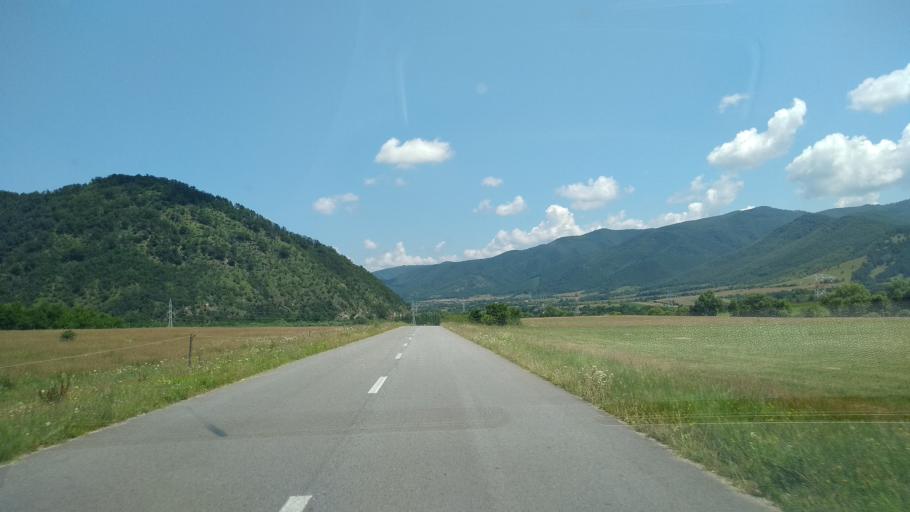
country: RO
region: Hunedoara
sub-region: Comuna Santamaria-Orlea
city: Santamaria-Orlea
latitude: 45.5867
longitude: 22.9778
